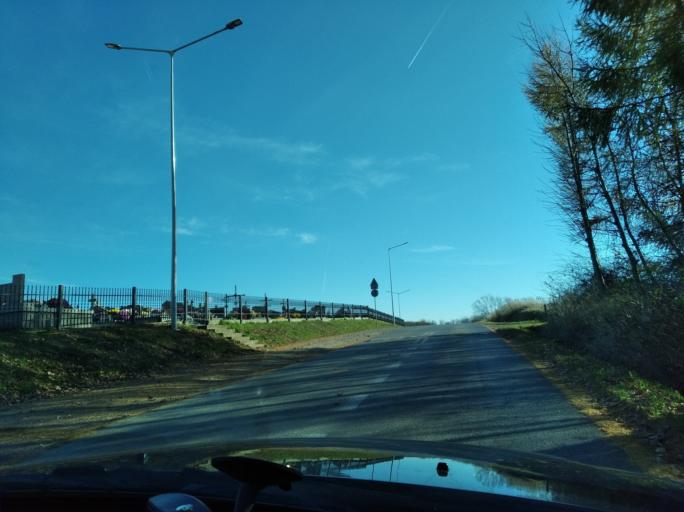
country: PL
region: Subcarpathian Voivodeship
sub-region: Powiat rzeszowski
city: Niechobrz
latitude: 49.9907
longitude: 21.8806
